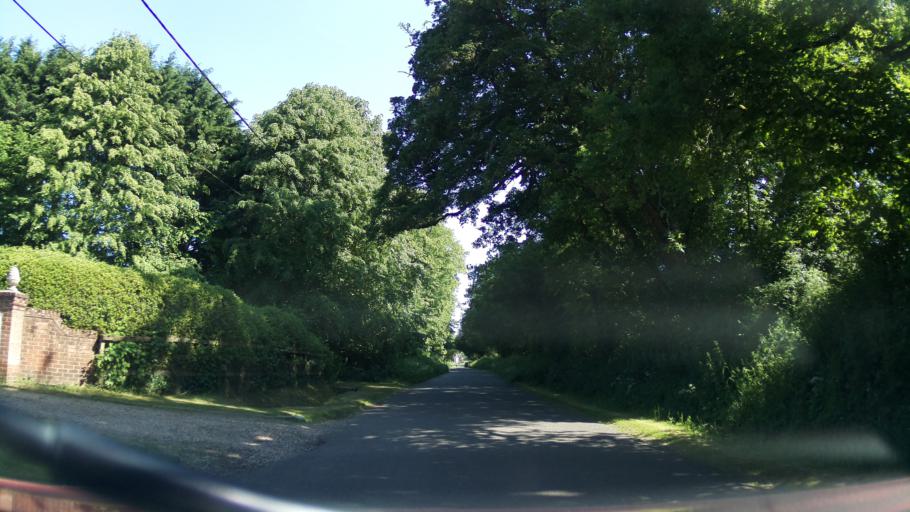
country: GB
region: England
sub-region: Hampshire
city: Abbotts Ann
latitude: 51.2528
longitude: -1.5761
